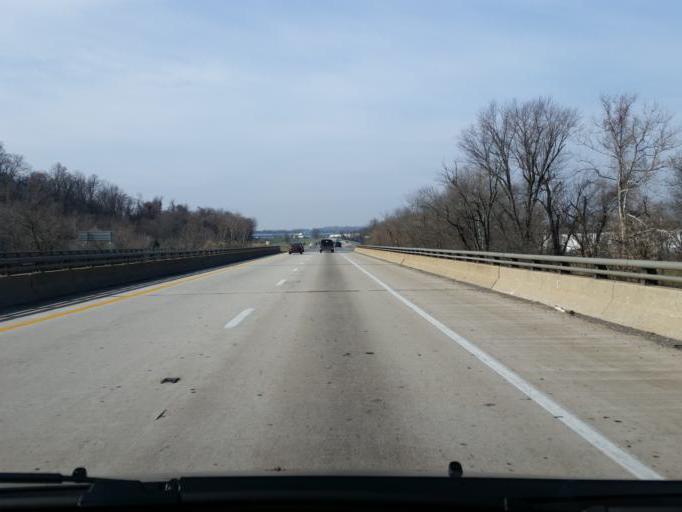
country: US
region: Pennsylvania
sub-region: Dauphin County
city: Middletown
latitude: 40.2260
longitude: -76.7264
